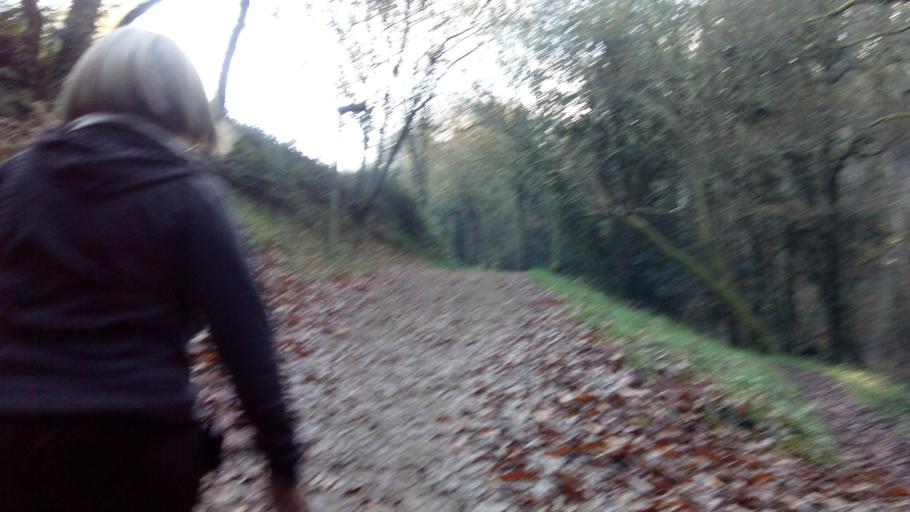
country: ES
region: Galicia
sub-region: Provincia de Pontevedra
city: Meis
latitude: 42.4878
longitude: -8.7521
